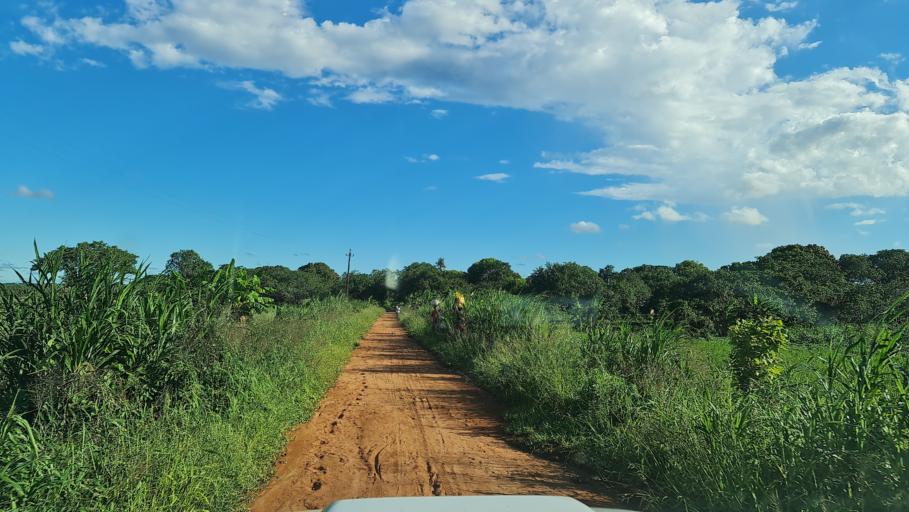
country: MZ
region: Nampula
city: Ilha de Mocambique
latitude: -14.9257
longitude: 40.2195
